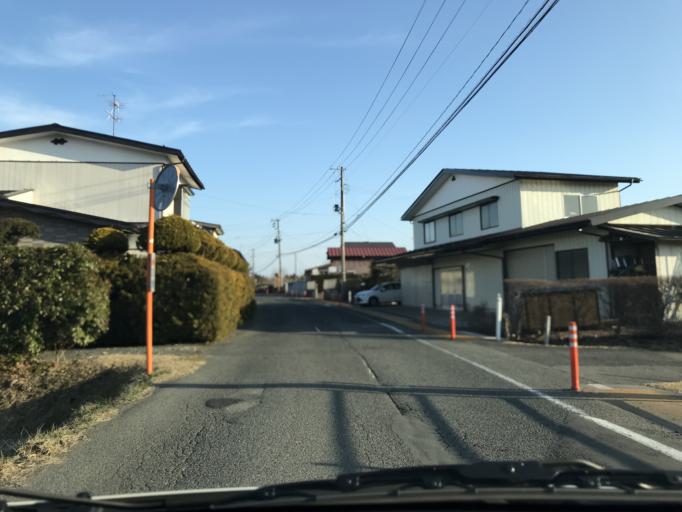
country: JP
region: Iwate
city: Kitakami
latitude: 39.2107
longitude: 141.1157
